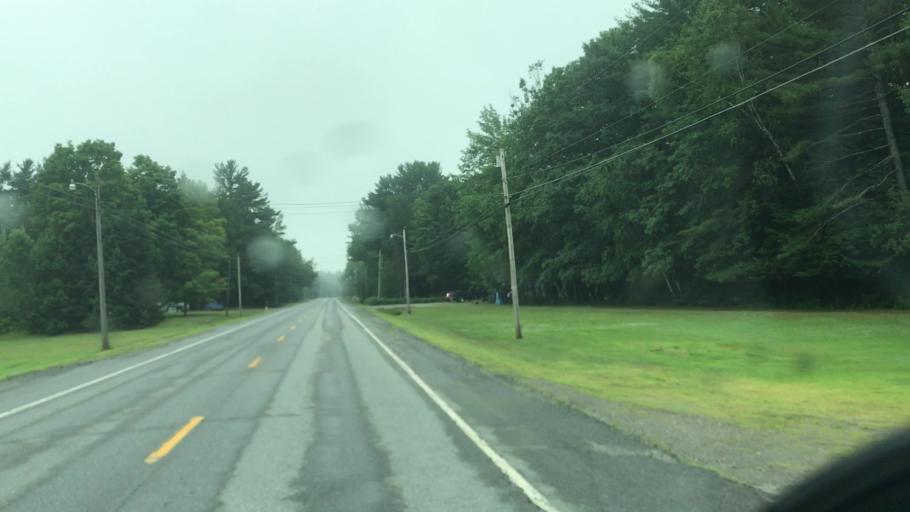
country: US
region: Maine
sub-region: Penobscot County
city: Howland
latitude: 45.2619
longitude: -68.6383
